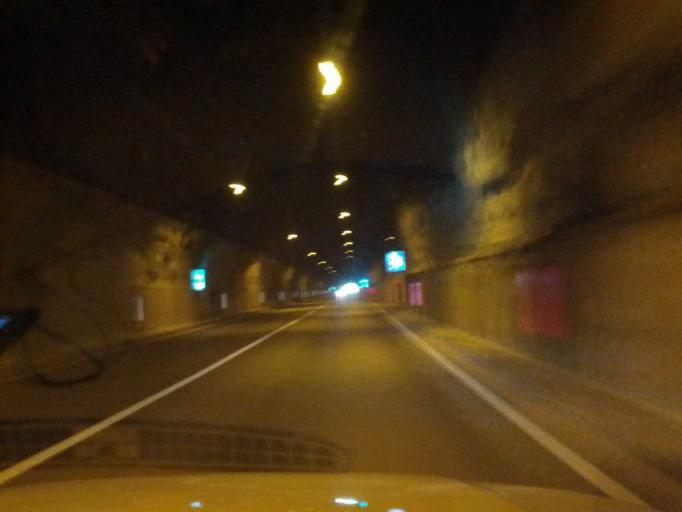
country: IT
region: Campania
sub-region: Provincia di Caserta
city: Mignano Monte Lungo
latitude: 41.4412
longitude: 14.0031
